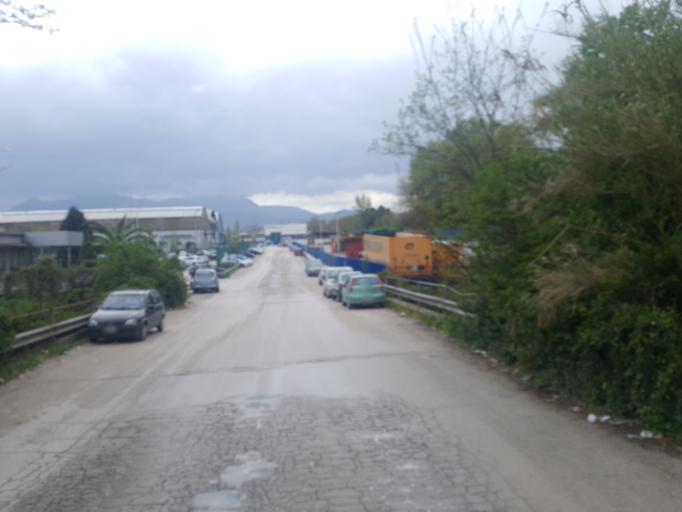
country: IT
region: Campania
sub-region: Provincia di Avellino
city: Atripalda
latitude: 40.9369
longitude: 14.8208
